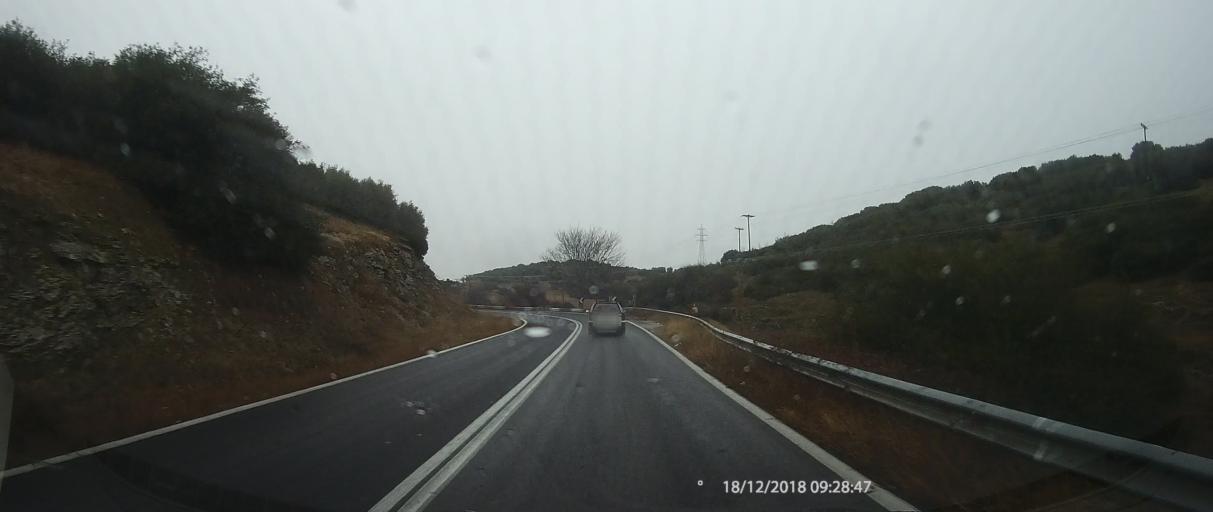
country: GR
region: Thessaly
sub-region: Nomos Larisis
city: Elassona
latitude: 39.9221
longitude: 22.1719
